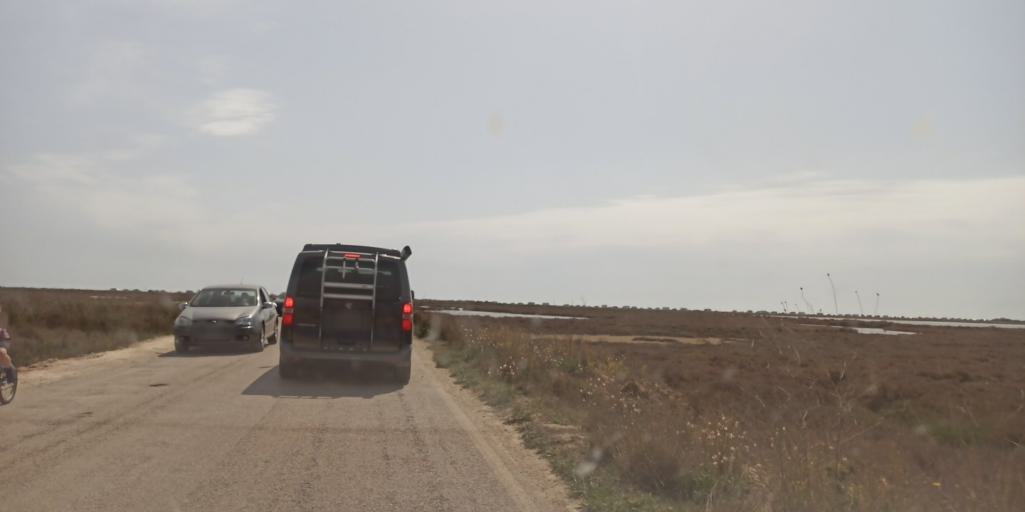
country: ES
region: Catalonia
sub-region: Provincia de Tarragona
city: Deltebre
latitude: 40.6391
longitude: 0.7421
